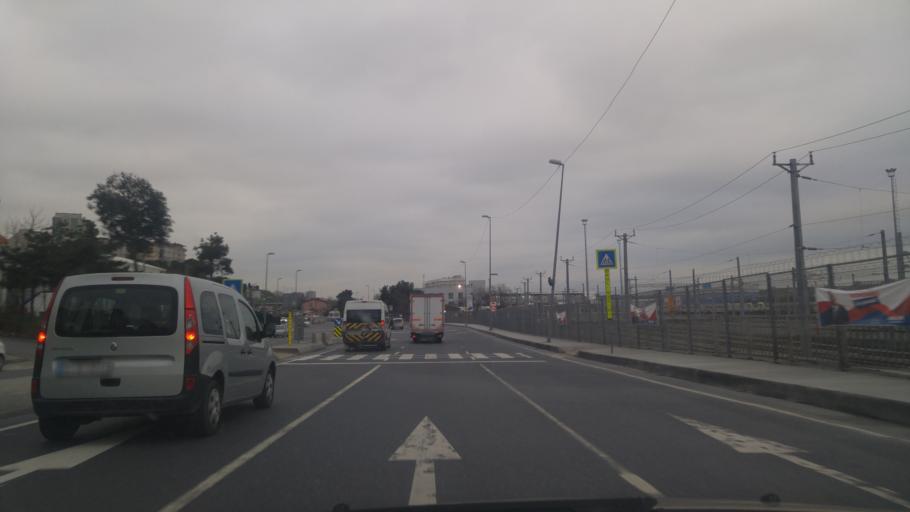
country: TR
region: Istanbul
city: Mahmutbey
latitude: 41.0222
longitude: 28.7674
